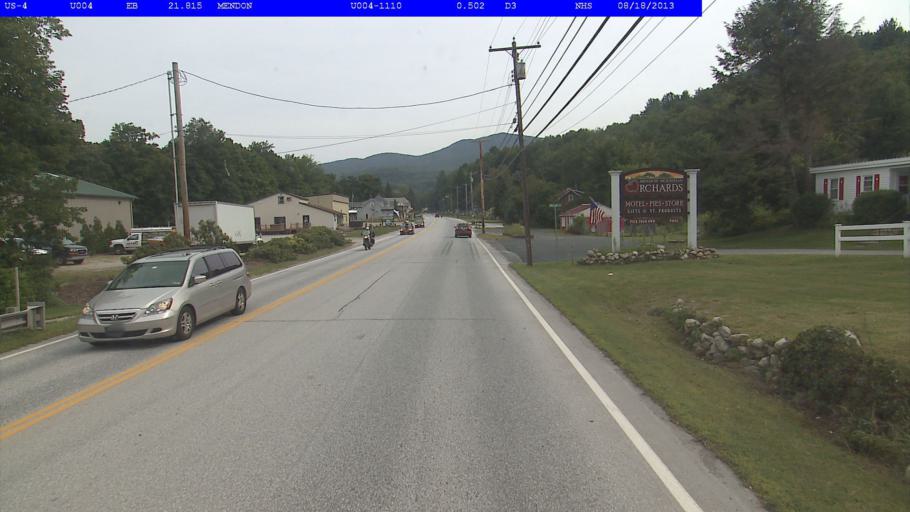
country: US
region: Vermont
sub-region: Rutland County
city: Rutland
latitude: 43.6410
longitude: -72.9321
